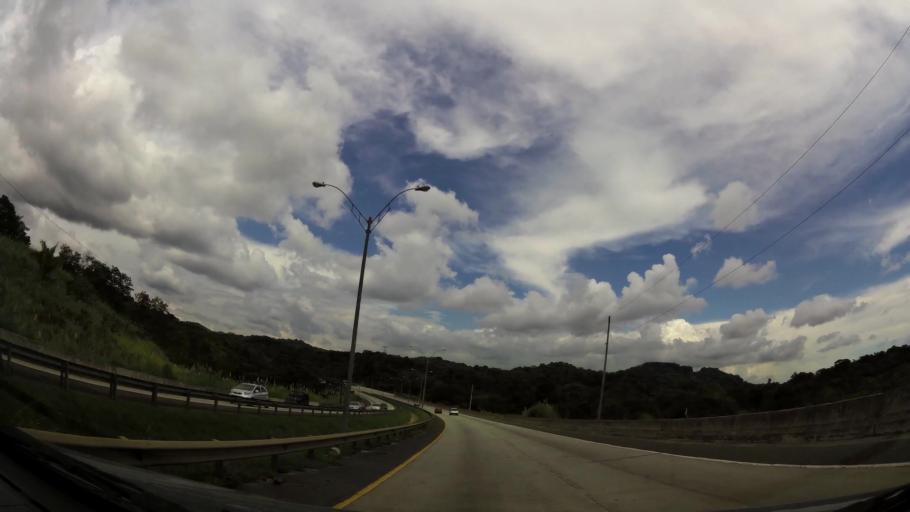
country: PA
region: Panama
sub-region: Distrito Arraijan
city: Arraijan
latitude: 8.9695
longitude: -79.6438
